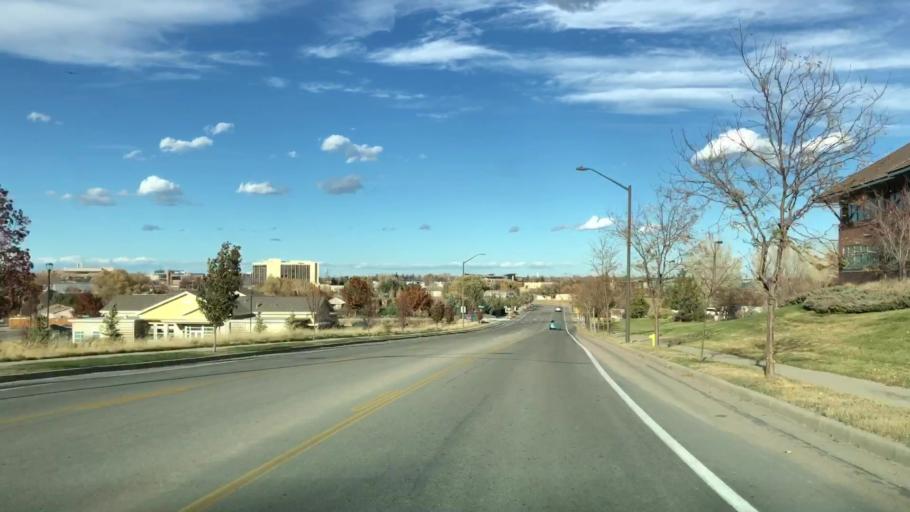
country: US
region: Colorado
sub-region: Larimer County
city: Fort Collins
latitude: 40.5591
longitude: -105.0868
